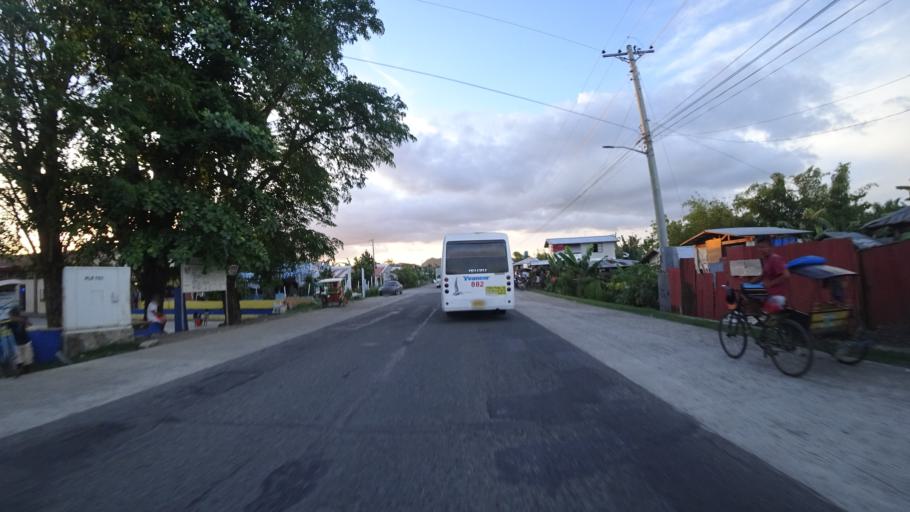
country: PH
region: Eastern Visayas
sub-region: Province of Leyte
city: Palo
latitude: 11.1469
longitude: 125.0018
